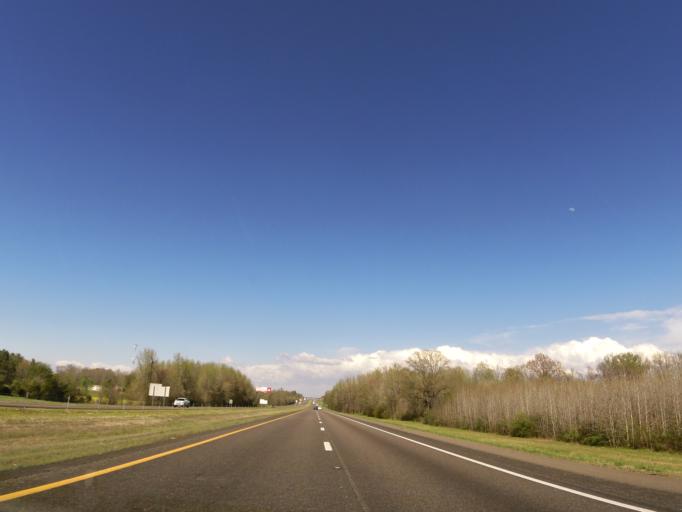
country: US
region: Tennessee
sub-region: Decatur County
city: Parsons
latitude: 35.8444
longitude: -88.0783
